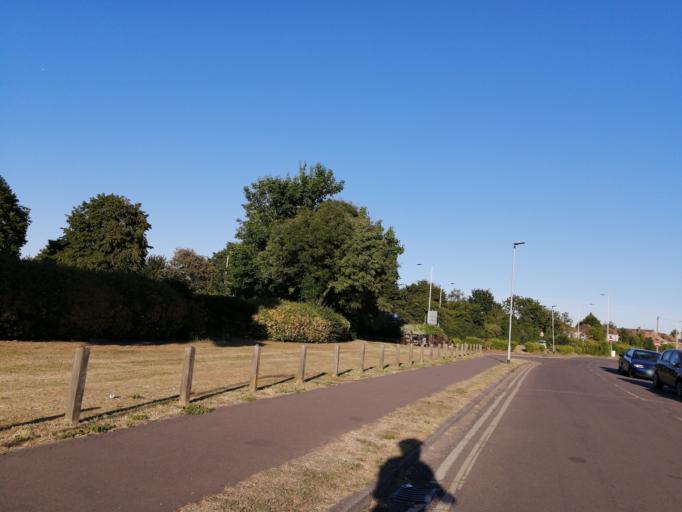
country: GB
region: England
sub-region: Peterborough
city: Marholm
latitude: 52.6077
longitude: -0.2749
